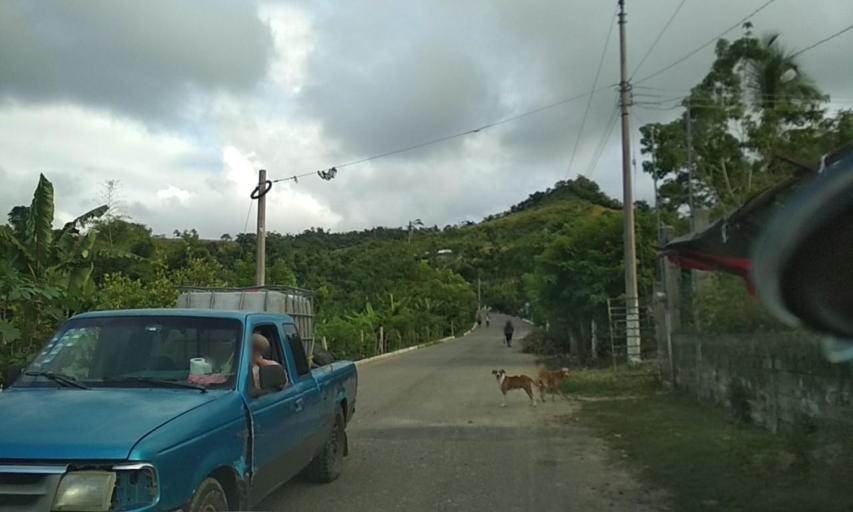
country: MX
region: Veracruz
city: Cazones de Herrera
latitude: 20.6401
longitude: -97.3379
